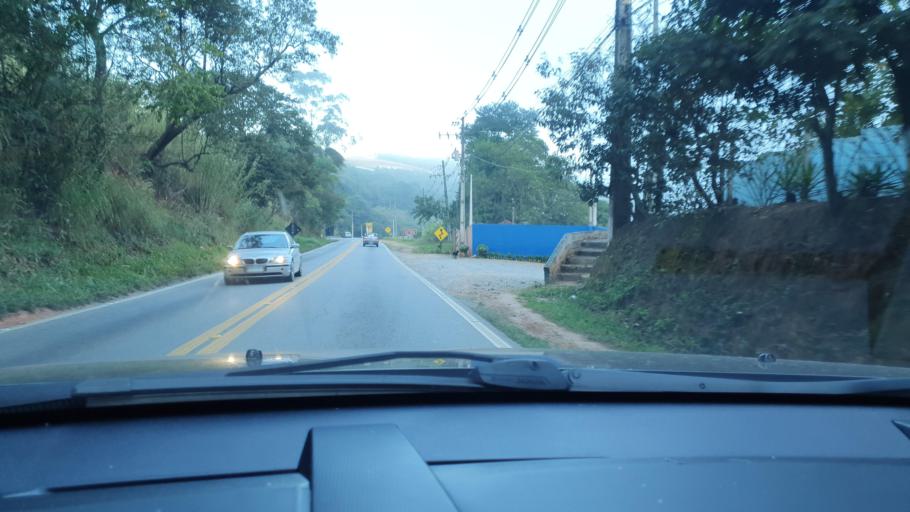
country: BR
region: Sao Paulo
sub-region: Ibiuna
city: Ibiuna
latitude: -23.6839
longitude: -47.2700
